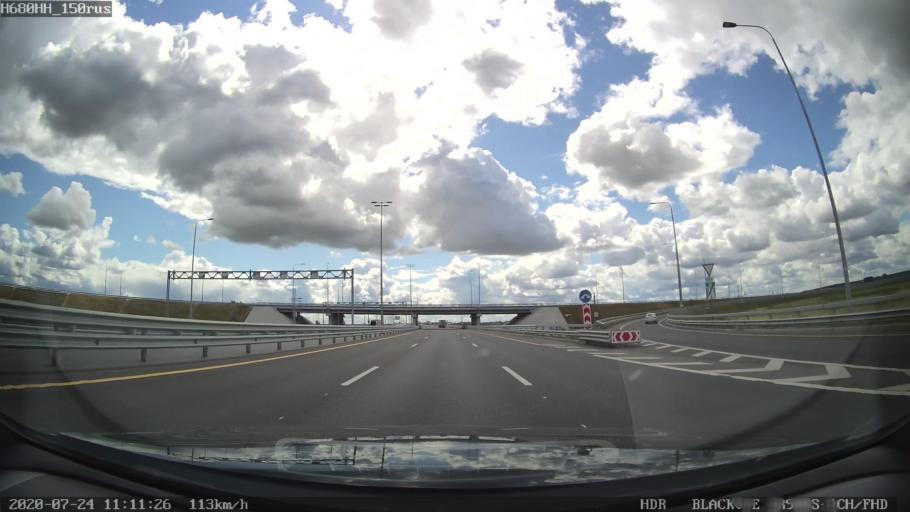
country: RU
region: Leningrad
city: Fedorovskoye
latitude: 59.7229
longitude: 30.5156
